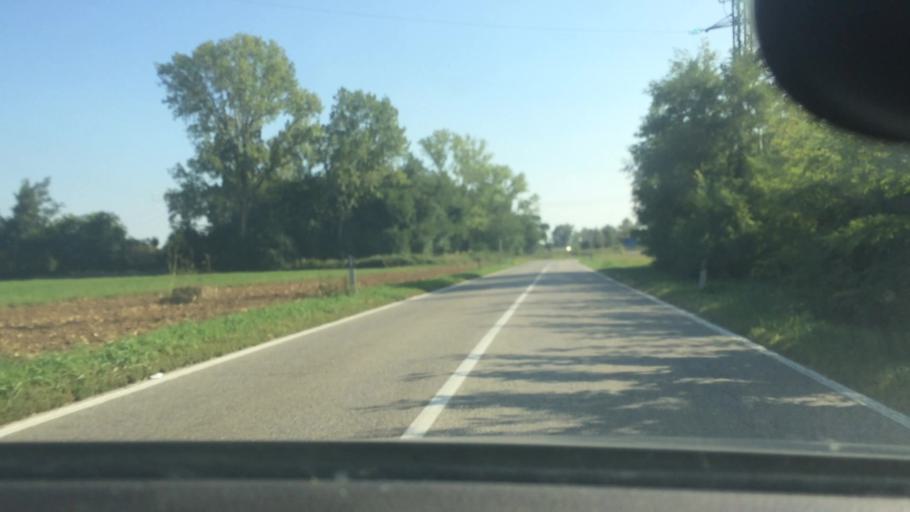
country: IT
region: Lombardy
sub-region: Citta metropolitana di Milano
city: Buscate
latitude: 45.5303
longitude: 8.8097
